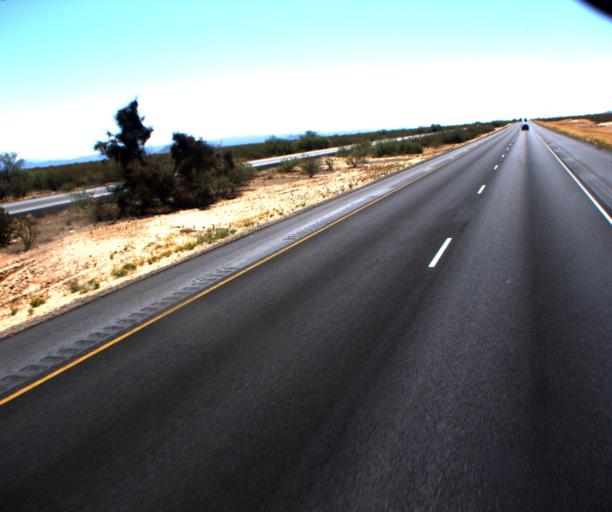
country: US
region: Arizona
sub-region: Yavapai County
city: Congress
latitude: 34.0802
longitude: -112.8891
